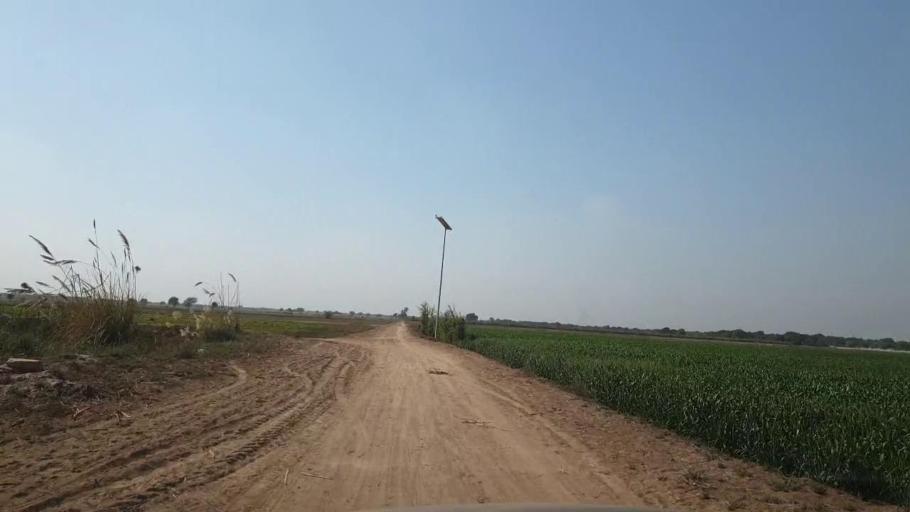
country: PK
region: Sindh
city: Tando Allahyar
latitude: 25.5617
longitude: 68.6977
